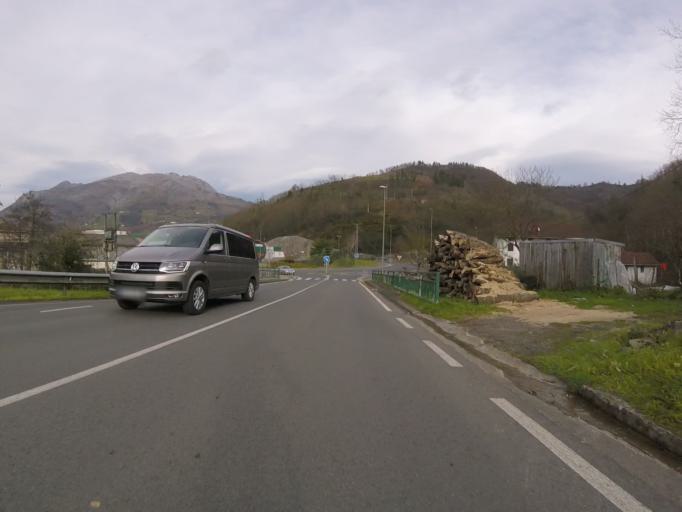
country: ES
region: Basque Country
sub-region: Provincia de Guipuzcoa
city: Azpeitia
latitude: 43.1747
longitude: -2.2516
